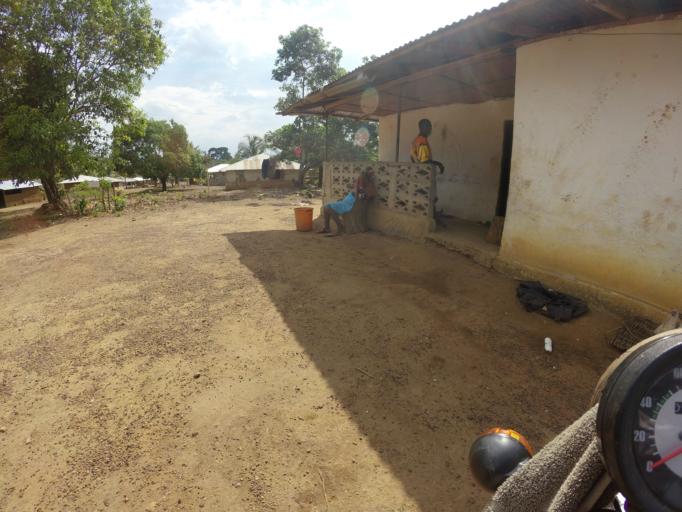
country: SL
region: Southern Province
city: Zimmi
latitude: 7.1506
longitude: -11.1946
